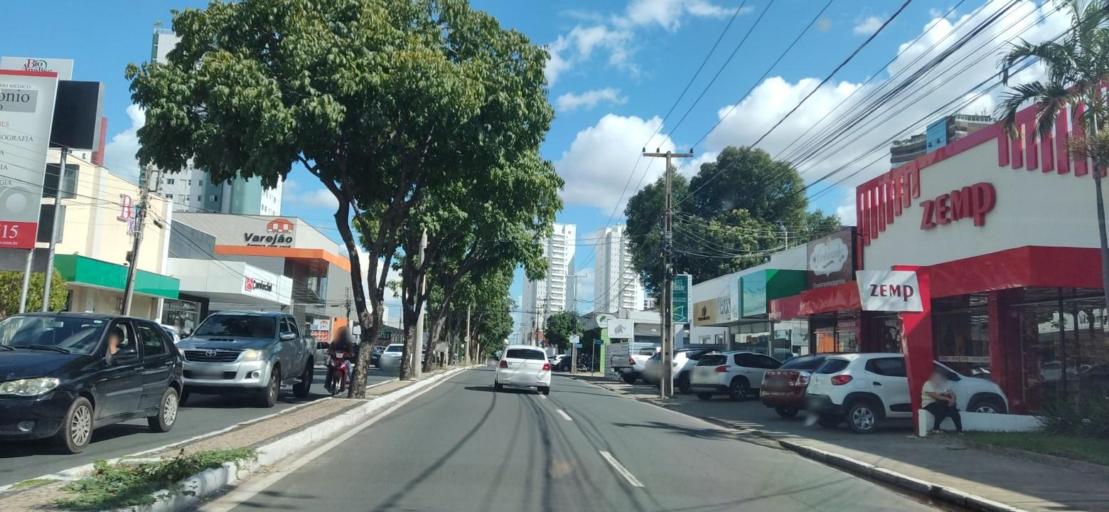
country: BR
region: Piaui
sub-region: Teresina
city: Teresina
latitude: -5.0733
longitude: -42.7916
